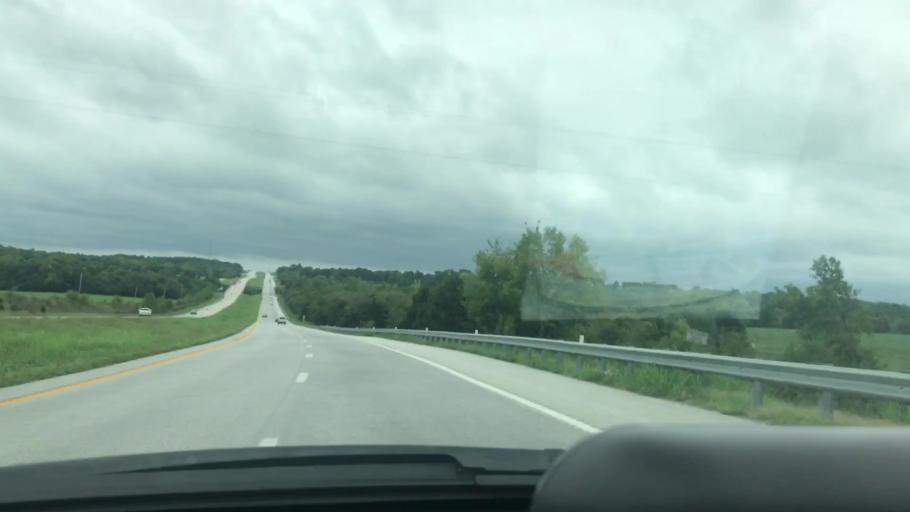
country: US
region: Missouri
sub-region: Greene County
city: Fair Grove
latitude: 37.4097
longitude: -93.1456
